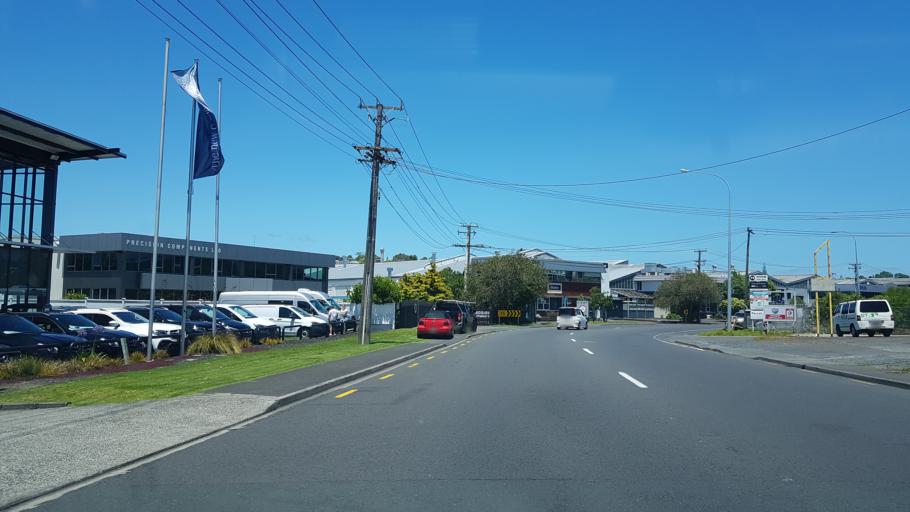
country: NZ
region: Auckland
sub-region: Auckland
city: North Shore
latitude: -36.7724
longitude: 174.7380
